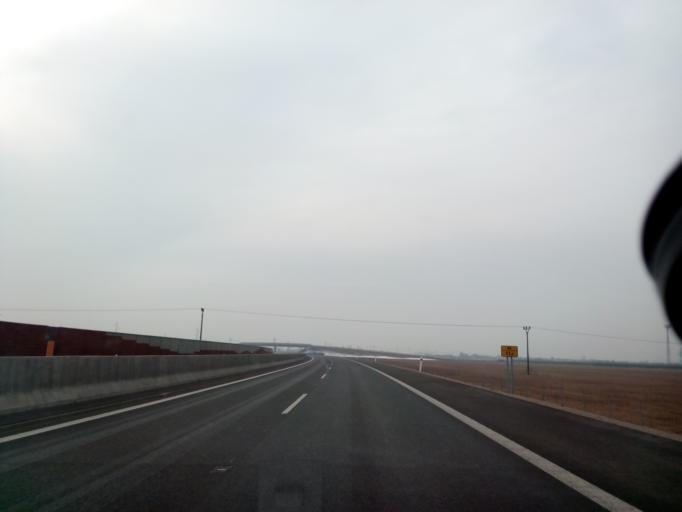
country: SK
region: Kosicky
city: Kosice
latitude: 48.6213
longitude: 21.2419
